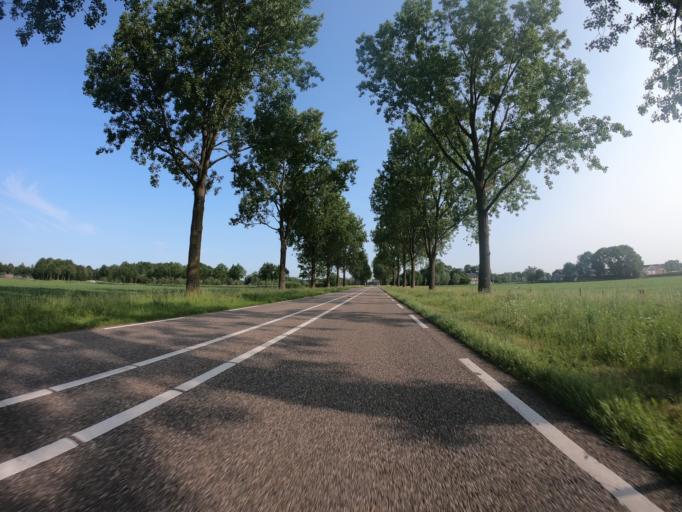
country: NL
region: North Brabant
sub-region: Gemeente Landerd
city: Reek
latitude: 51.7673
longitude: 5.6685
